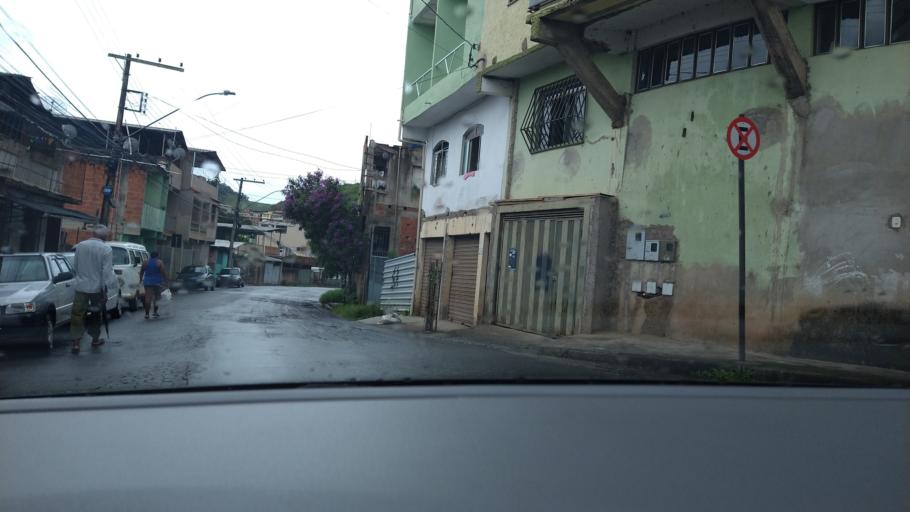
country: BR
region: Minas Gerais
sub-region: Ponte Nova
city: Ponte Nova
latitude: -20.4051
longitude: -42.8958
